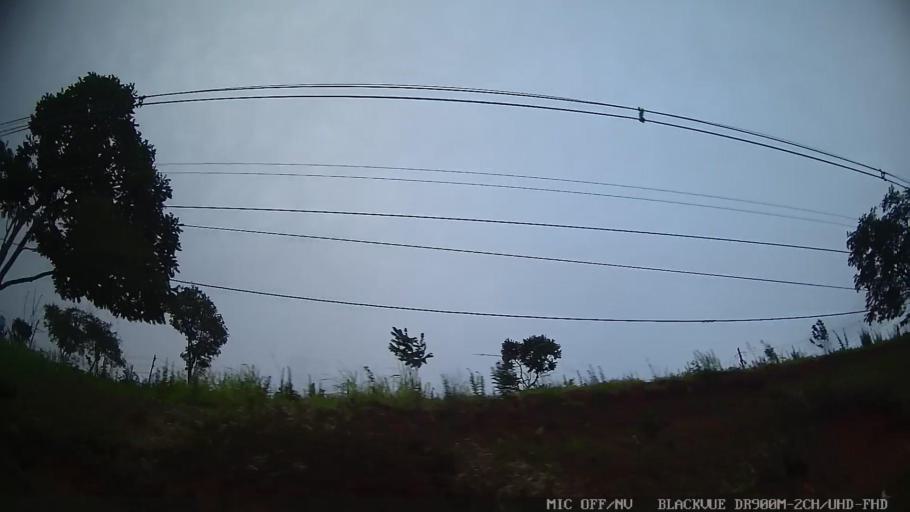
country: BR
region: Sao Paulo
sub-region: Braganca Paulista
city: Braganca Paulista
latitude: -22.9500
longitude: -46.5535
